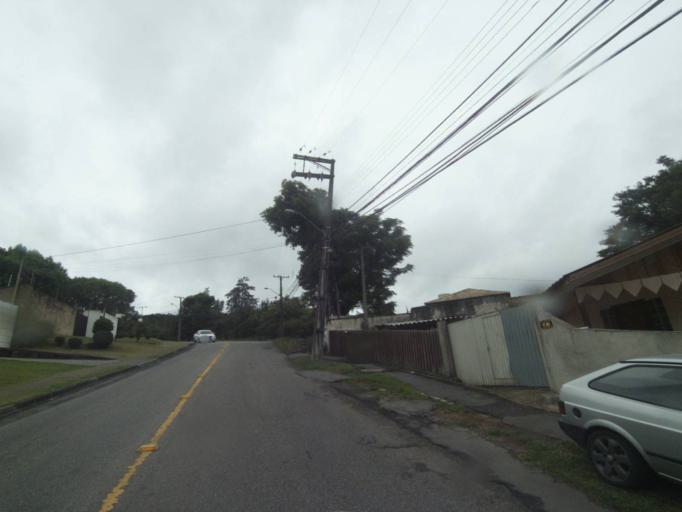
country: BR
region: Parana
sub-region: Curitiba
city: Curitiba
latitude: -25.4274
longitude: -49.3255
